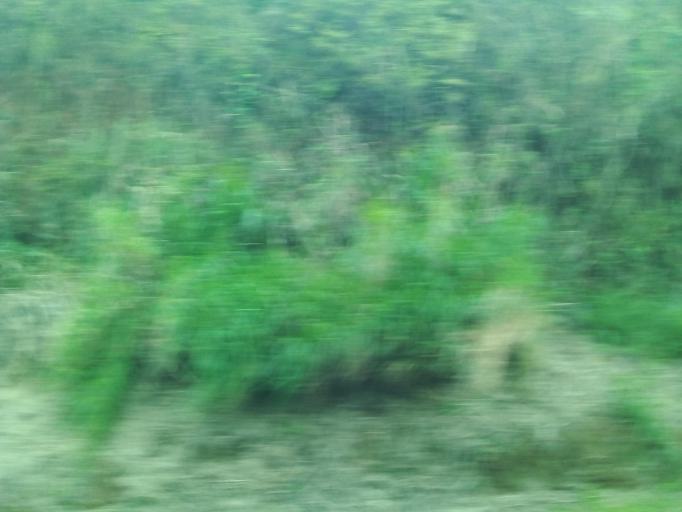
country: BR
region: Minas Gerais
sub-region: Nova Era
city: Nova Era
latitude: -19.7415
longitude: -43.0185
